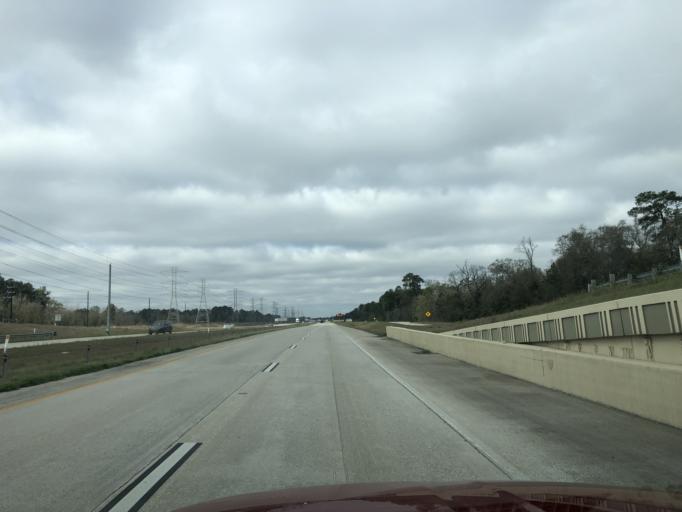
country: US
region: Texas
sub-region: Harris County
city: Spring
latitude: 30.0894
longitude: -95.4582
